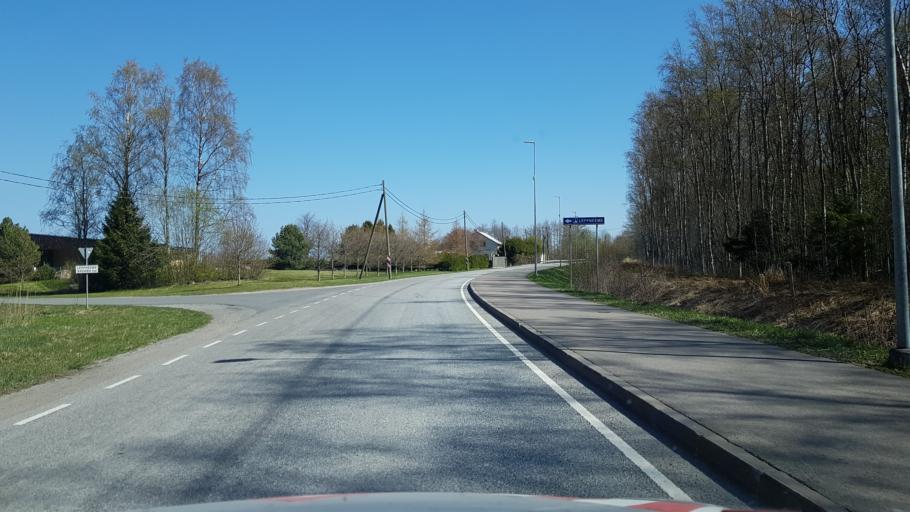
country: EE
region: Harju
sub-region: Viimsi vald
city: Viimsi
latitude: 59.5476
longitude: 24.8647
